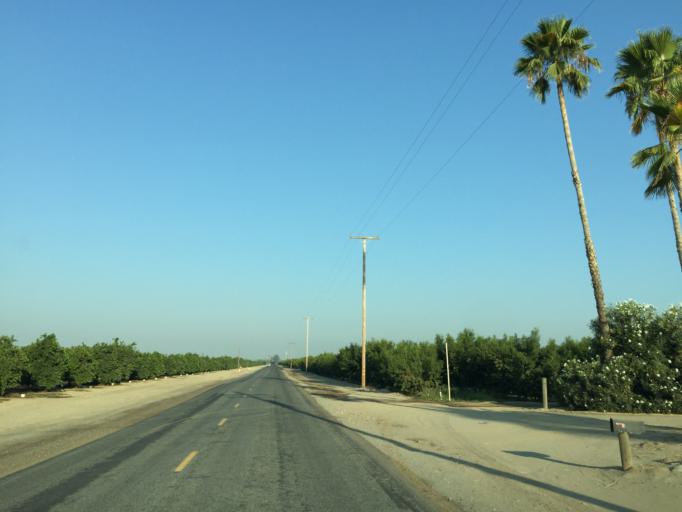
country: US
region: California
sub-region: Tulare County
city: London
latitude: 36.4589
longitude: -119.4589
